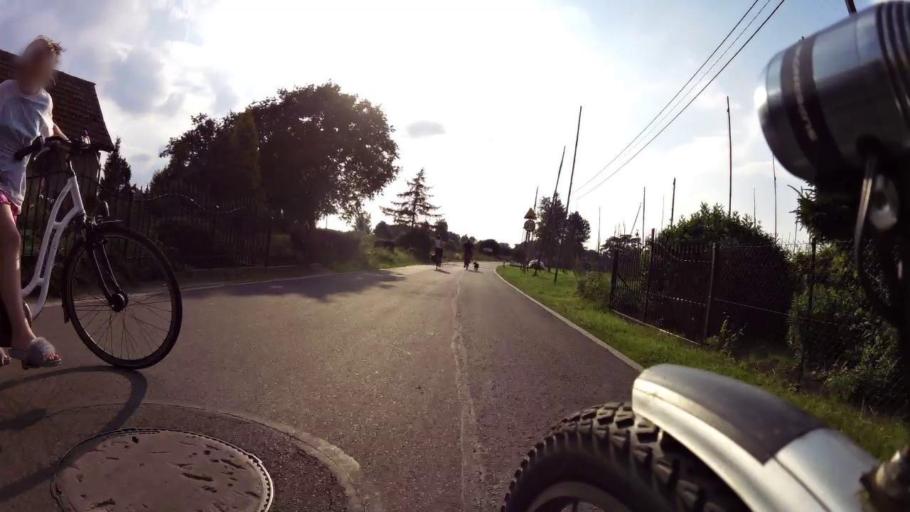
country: PL
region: West Pomeranian Voivodeship
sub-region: Powiat goleniowski
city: Stepnica
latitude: 53.6565
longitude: 14.5215
